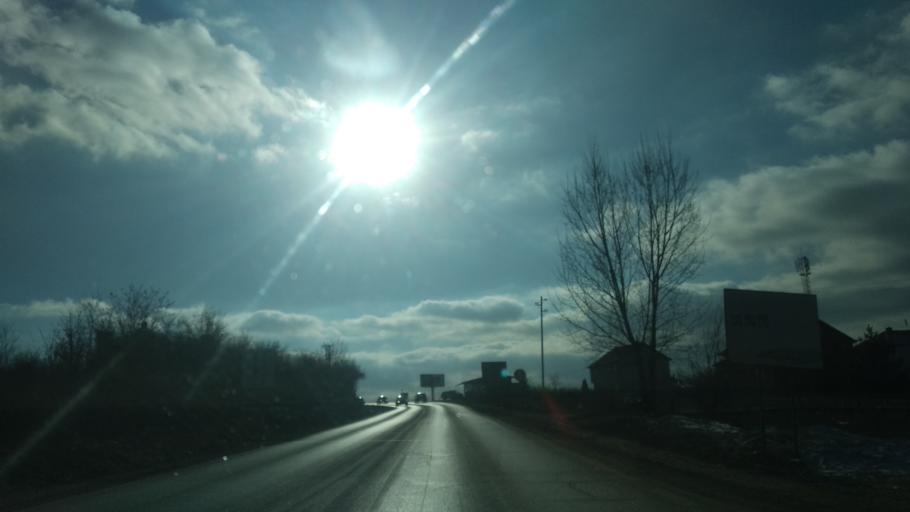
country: XK
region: Pristina
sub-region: Komuna e Prishtines
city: Pristina
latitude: 42.7460
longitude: 21.1403
